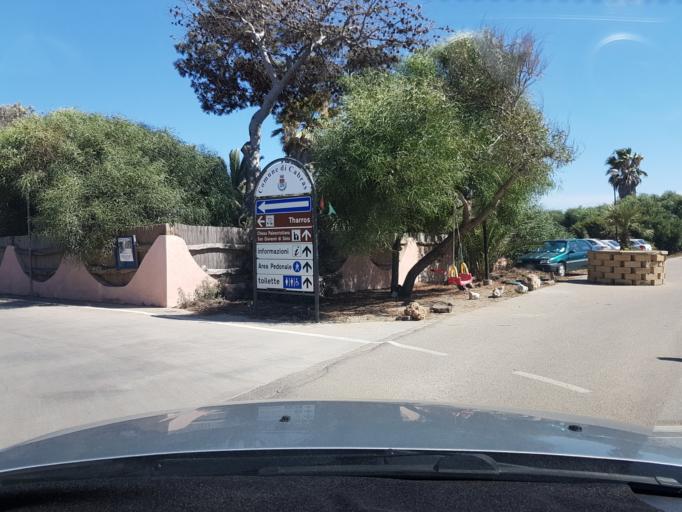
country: IT
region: Sardinia
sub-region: Provincia di Oristano
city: Cabras
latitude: 39.8833
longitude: 8.4384
